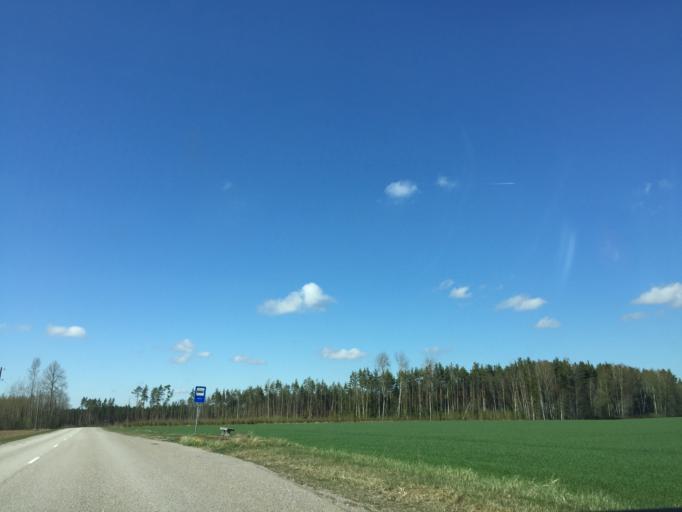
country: LV
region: Strenci
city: Seda
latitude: 57.5818
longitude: 25.7557
